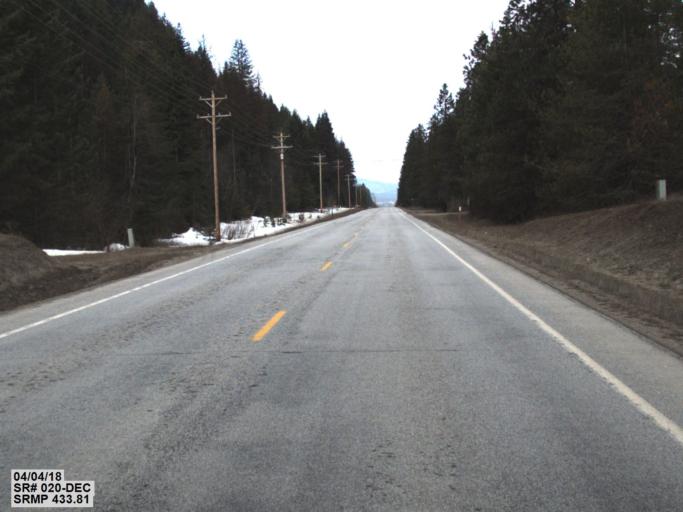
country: US
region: Washington
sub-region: Pend Oreille County
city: Newport
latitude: 48.2169
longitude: -117.0819
